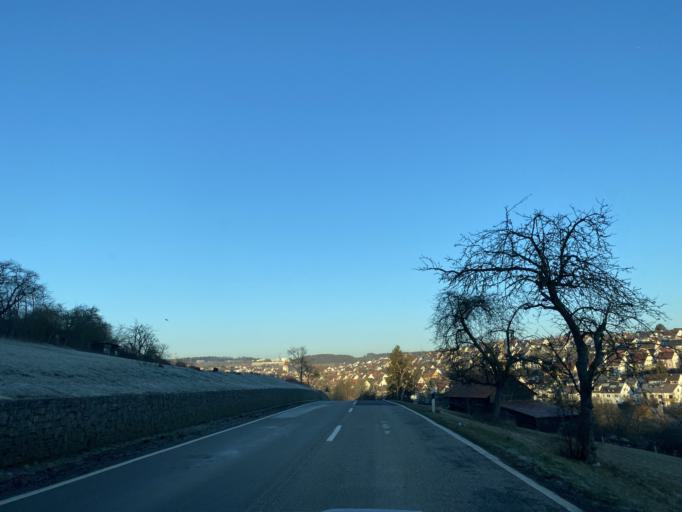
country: DE
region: Baden-Wuerttemberg
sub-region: Regierungsbezirk Stuttgart
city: Weissach
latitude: 48.8458
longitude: 8.9394
